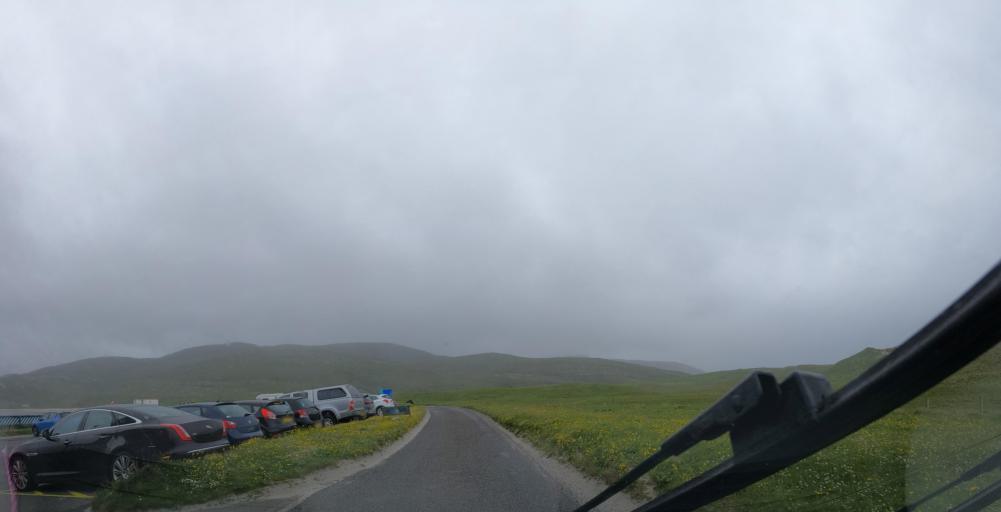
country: GB
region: Scotland
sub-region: Eilean Siar
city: Barra
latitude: 57.0254
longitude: -7.4501
